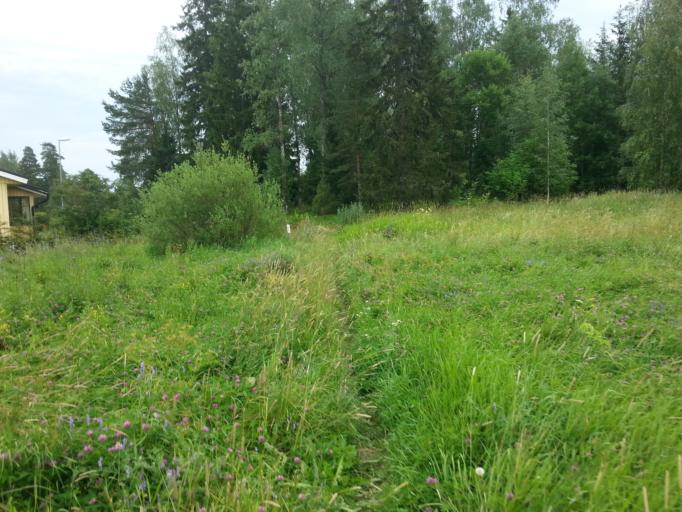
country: FI
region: Uusimaa
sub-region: Helsinki
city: Jaervenpaeae
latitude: 60.4968
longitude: 25.0769
